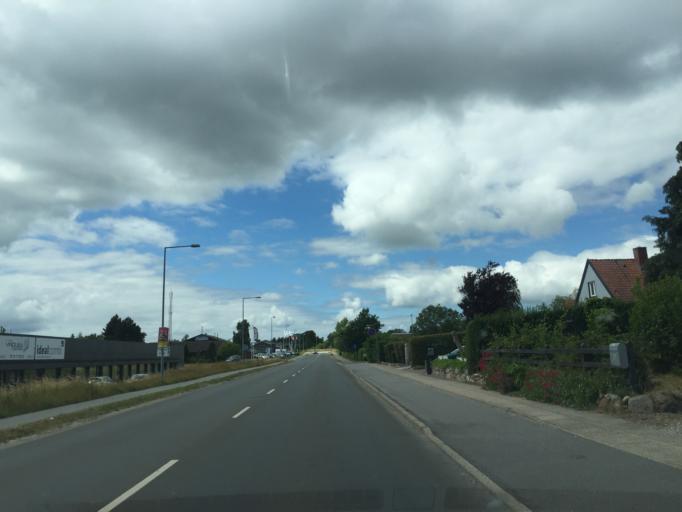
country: DK
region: South Denmark
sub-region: Svendborg Kommune
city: Svendborg
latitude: 55.0689
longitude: 10.5742
